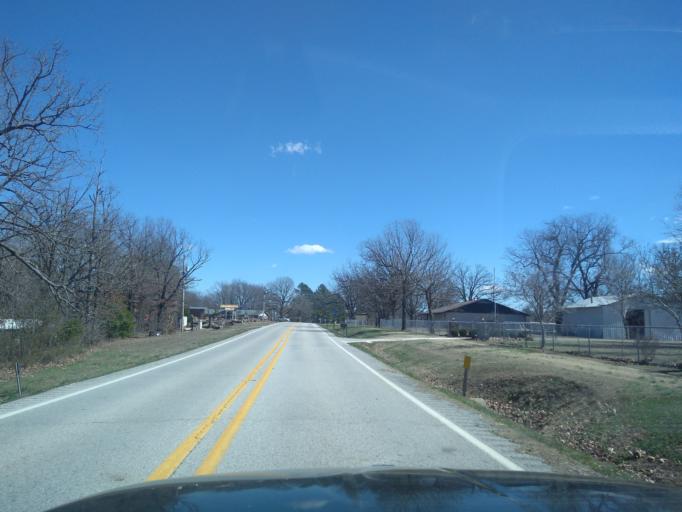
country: US
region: Arkansas
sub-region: Washington County
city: Farmington
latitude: 36.0808
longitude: -94.3029
